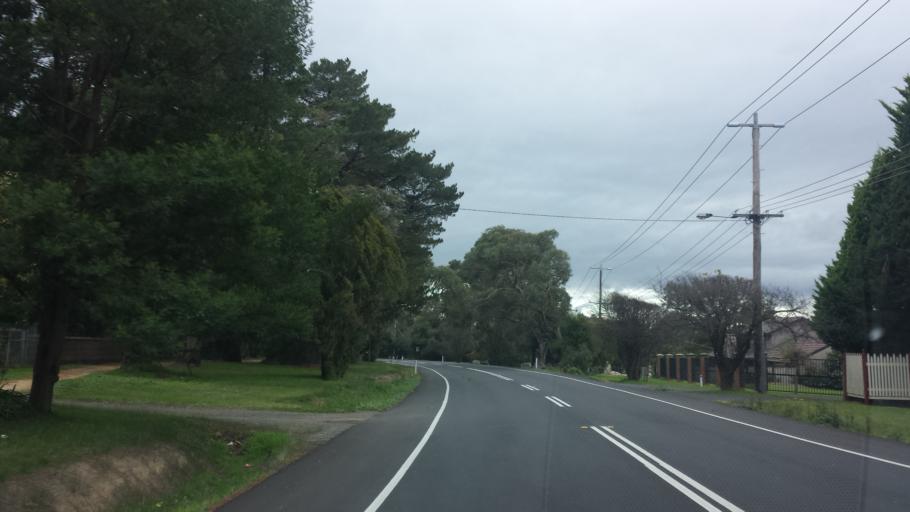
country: AU
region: Victoria
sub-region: Casey
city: Narre Warren North
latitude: -37.9857
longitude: 145.3043
